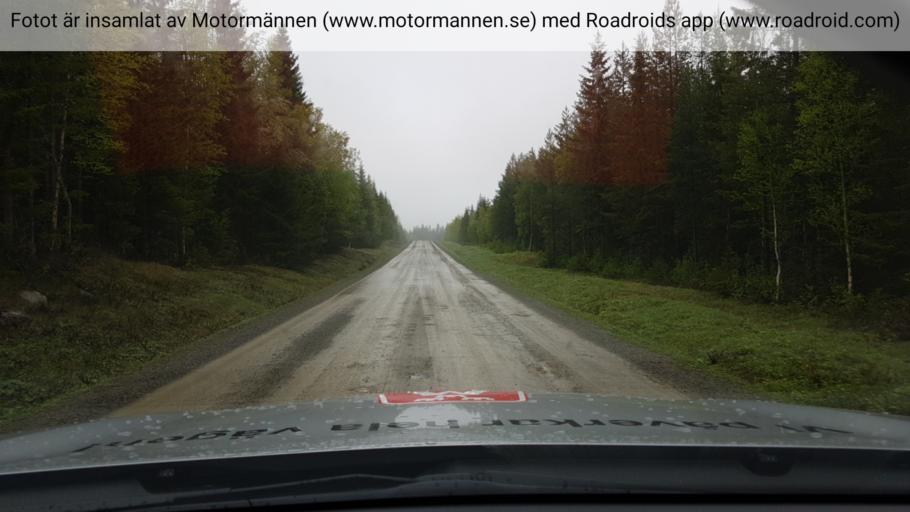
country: SE
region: Jaemtland
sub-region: Bergs Kommun
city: Hoverberg
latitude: 62.9988
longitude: 14.1480
